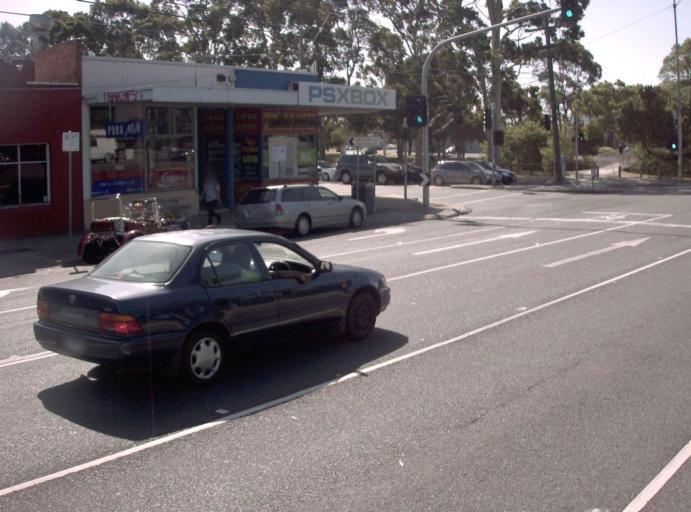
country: AU
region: Victoria
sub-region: Greater Dandenong
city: Dandenong
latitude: -37.9931
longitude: 145.2162
